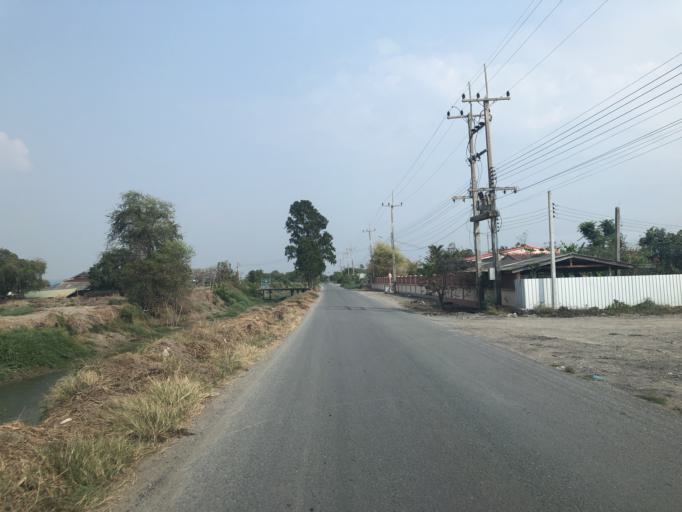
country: TH
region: Chachoengsao
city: Bang Pakong
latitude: 13.5103
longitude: 100.9315
